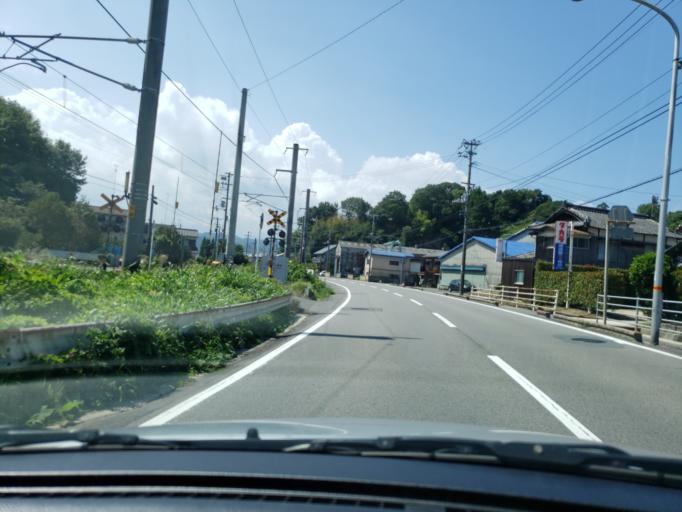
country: JP
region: Ehime
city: Hojo
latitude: 34.0858
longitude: 132.9295
